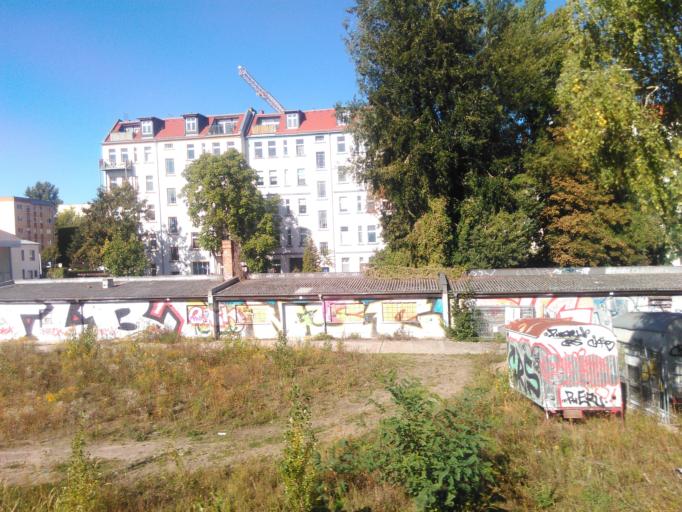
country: DE
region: Berlin
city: Treptow Bezirk
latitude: 52.4990
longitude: 13.4678
